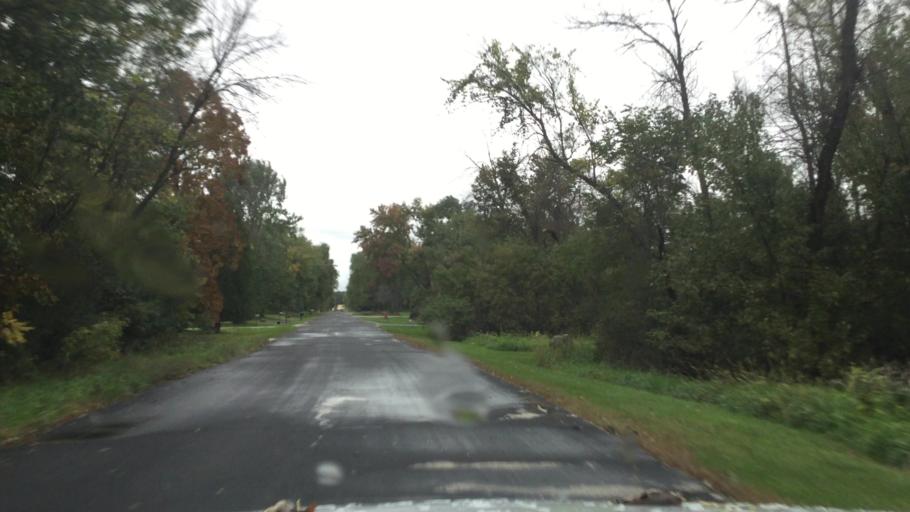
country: US
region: Wisconsin
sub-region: Racine County
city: Waterford
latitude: 42.7575
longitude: -88.1850
